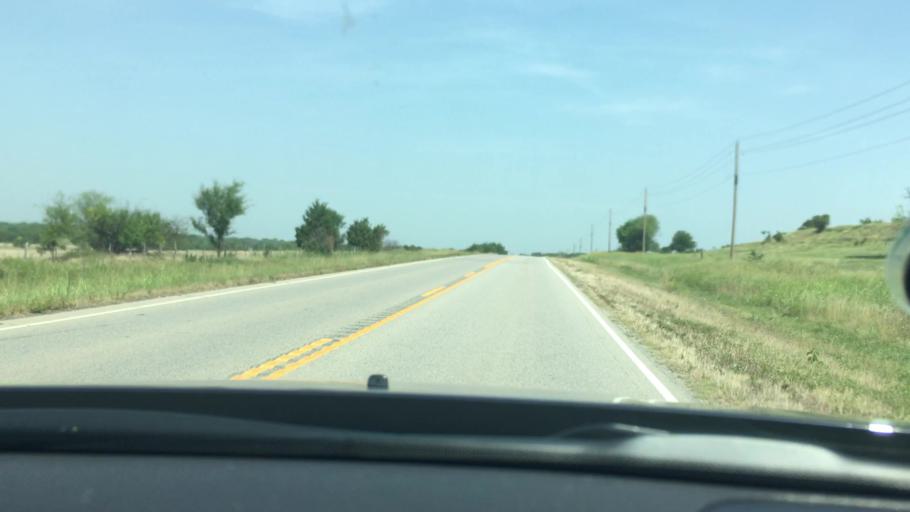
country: US
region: Oklahoma
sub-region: Coal County
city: Coalgate
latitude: 34.4554
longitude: -96.2124
